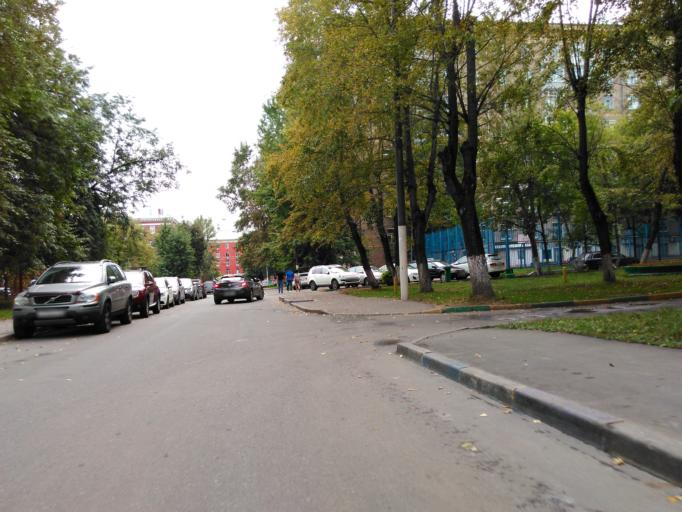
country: RU
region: Moskovskaya
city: Leninskiye Gory
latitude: 55.6823
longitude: 37.5699
